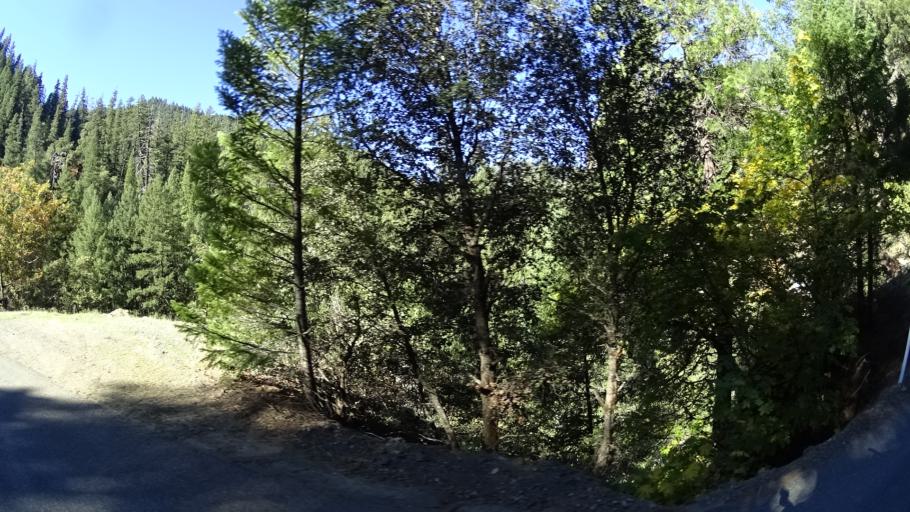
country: US
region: California
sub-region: Humboldt County
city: Willow Creek
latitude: 41.1448
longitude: -123.1939
